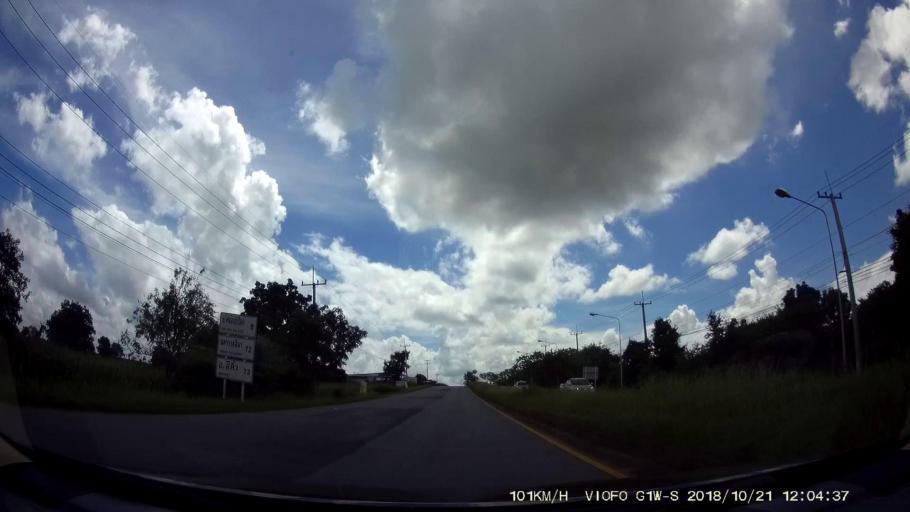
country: TH
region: Chaiyaphum
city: Chatturat
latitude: 15.4919
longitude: 101.8216
